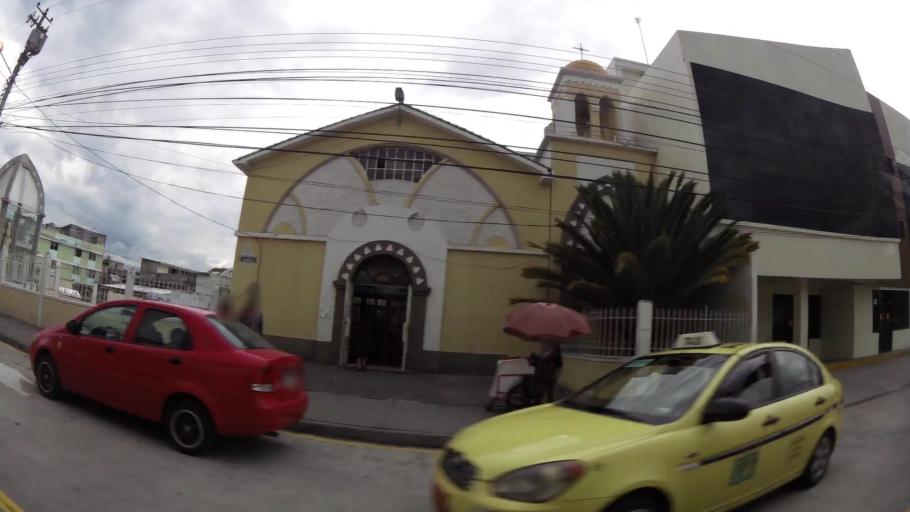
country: EC
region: Tungurahua
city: Ambato
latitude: -1.2335
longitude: -78.6164
